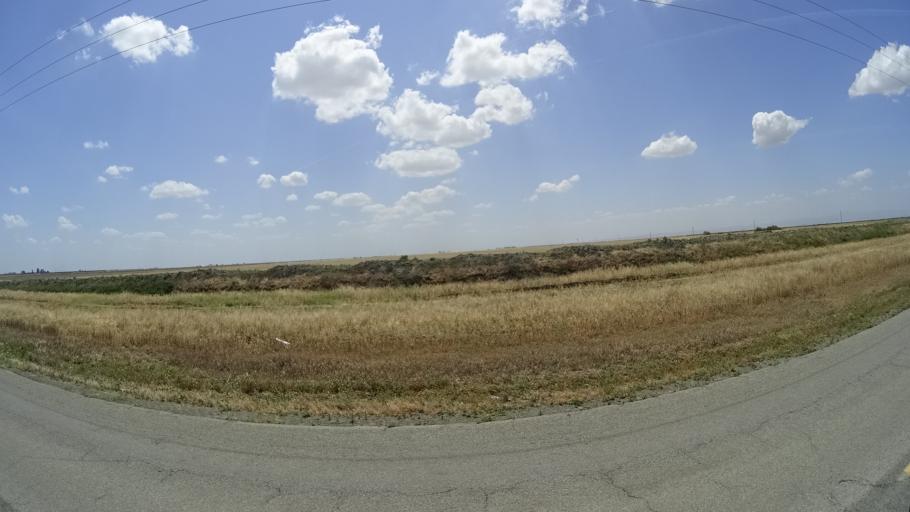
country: US
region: California
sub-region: Kings County
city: Stratford
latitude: 36.1895
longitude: -119.8759
